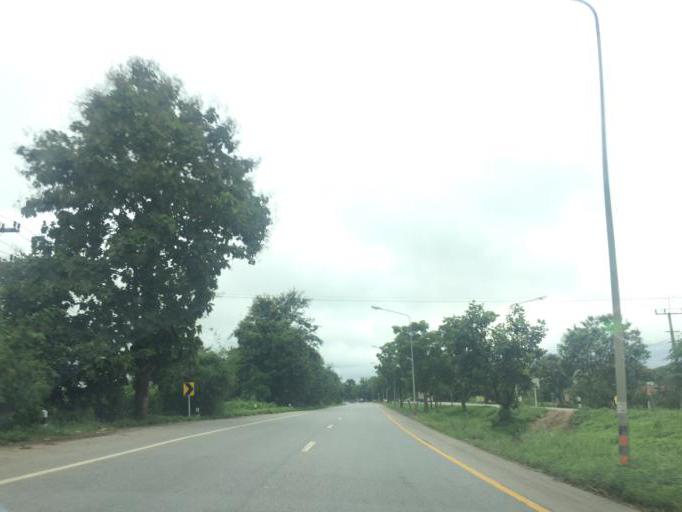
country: TH
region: Chiang Rai
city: Mae Lao
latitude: 19.7944
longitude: 99.7493
